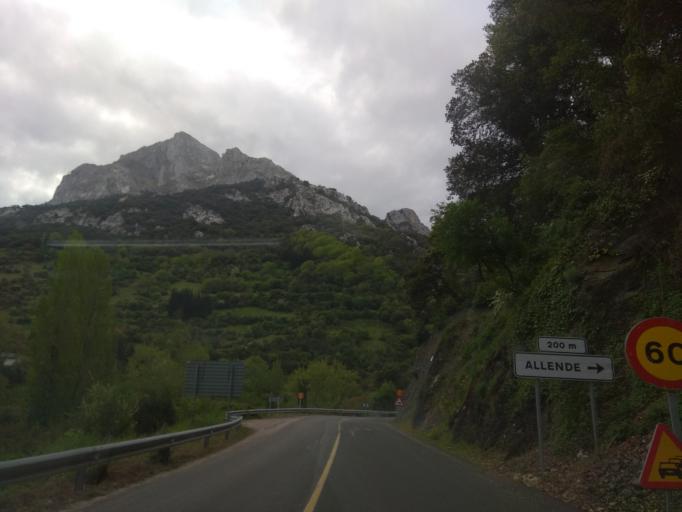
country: ES
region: Cantabria
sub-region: Provincia de Cantabria
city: Potes
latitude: 43.2145
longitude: -4.5925
